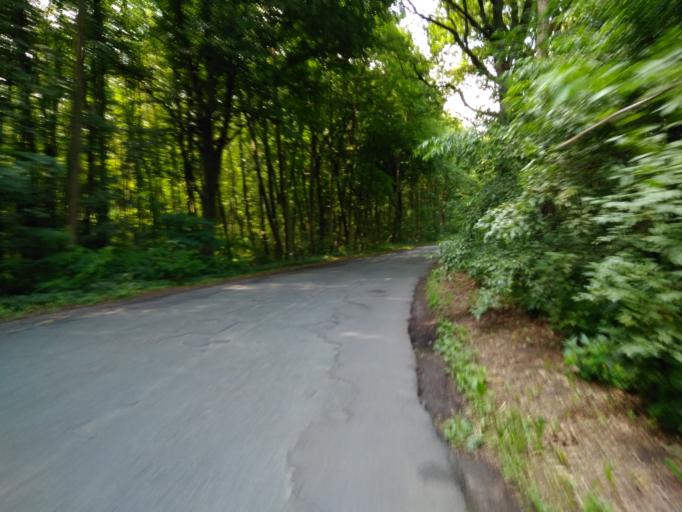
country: DE
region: North Rhine-Westphalia
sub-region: Regierungsbezirk Dusseldorf
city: Schermbeck
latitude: 51.6740
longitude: 6.9137
